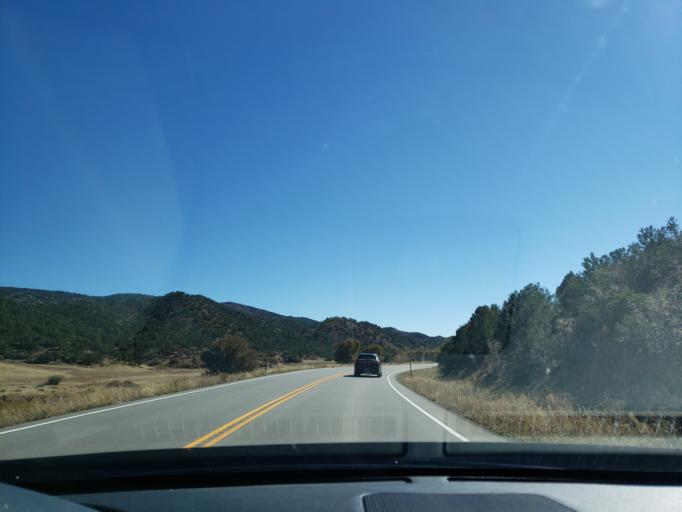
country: US
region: Colorado
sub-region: Fremont County
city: Canon City
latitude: 38.6025
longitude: -105.4316
